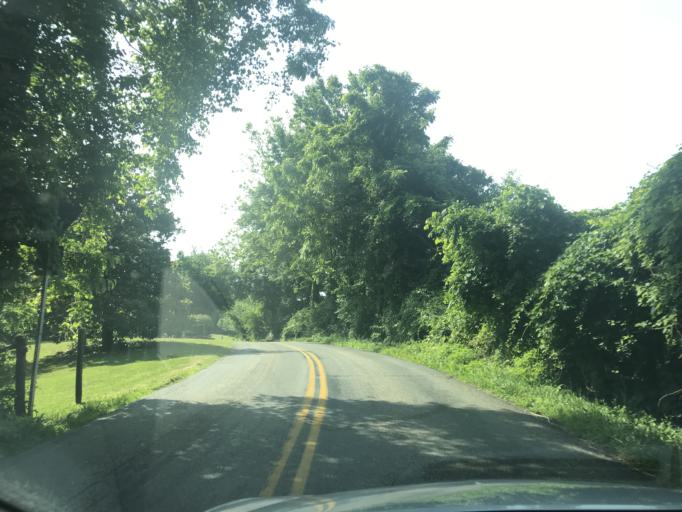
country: US
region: Maryland
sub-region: Harford County
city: Bel Air North
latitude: 39.5584
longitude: -76.4149
